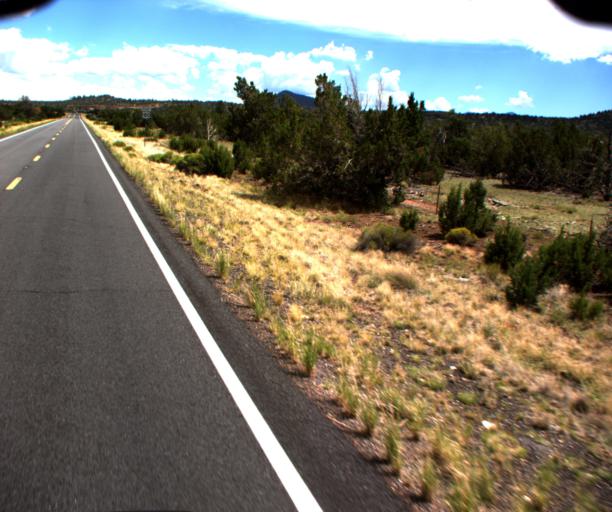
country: US
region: Arizona
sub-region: Coconino County
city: Parks
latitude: 35.5684
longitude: -111.9192
